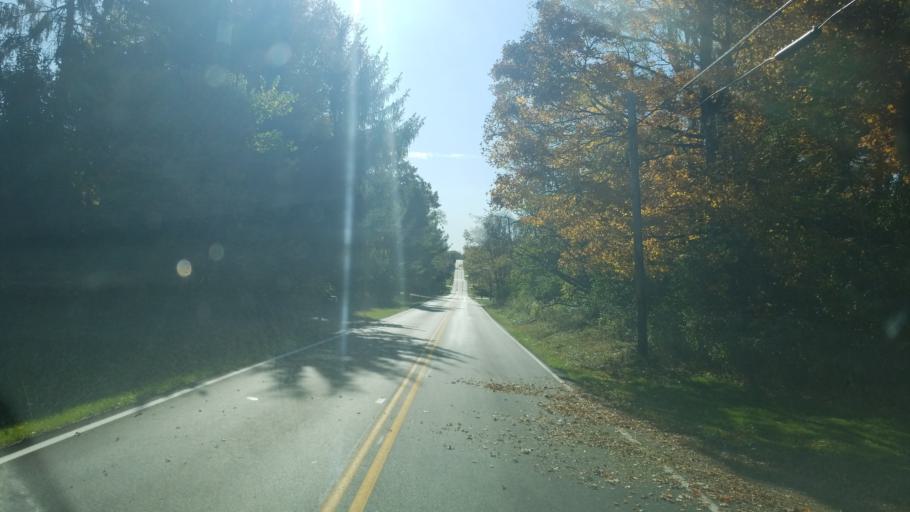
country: US
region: Ohio
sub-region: Warren County
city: Morrow
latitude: 39.3778
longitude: -84.0707
